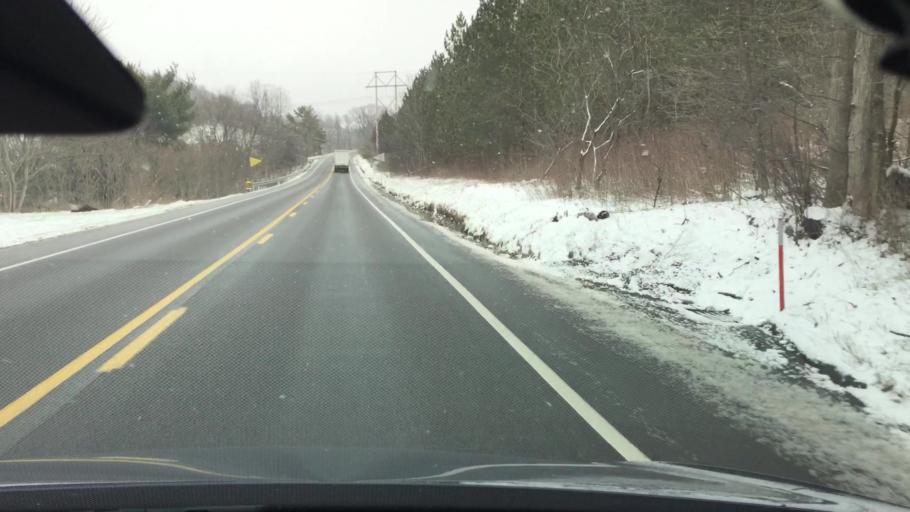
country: US
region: Pennsylvania
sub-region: Jefferson County
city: Brookville
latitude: 41.0495
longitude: -79.2528
